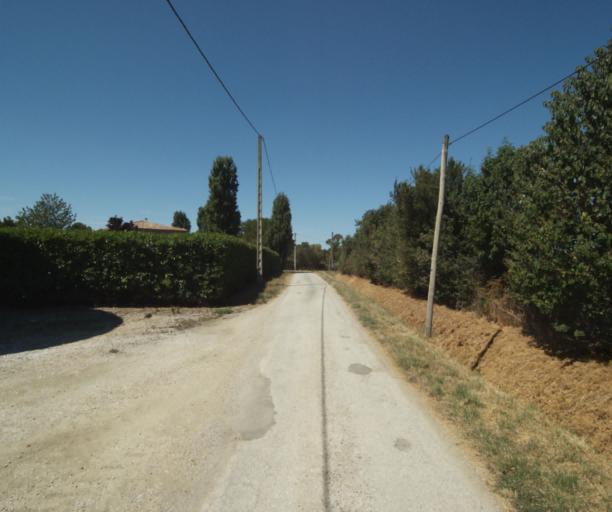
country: FR
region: Midi-Pyrenees
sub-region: Departement de la Haute-Garonne
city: Saint-Felix-Lauragais
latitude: 43.4713
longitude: 1.9417
